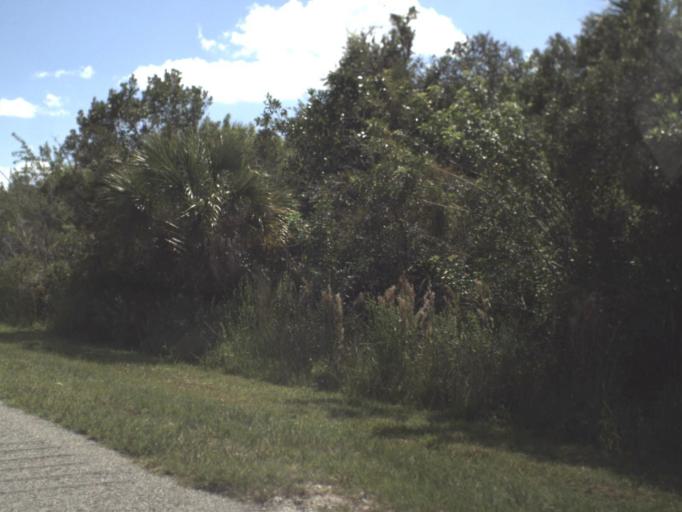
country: US
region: Florida
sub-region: Collier County
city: Marco
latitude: 25.9569
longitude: -81.4897
